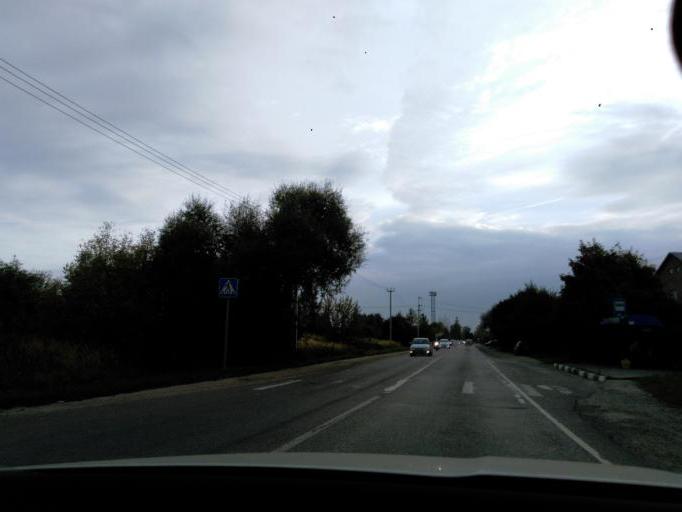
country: RU
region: Moskovskaya
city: Sheremet'yevskiy
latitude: 55.9690
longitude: 37.4791
